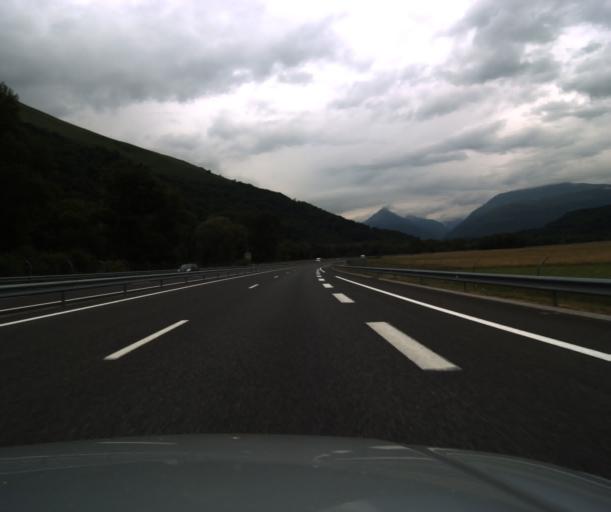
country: FR
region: Midi-Pyrenees
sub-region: Departement des Hautes-Pyrenees
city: Argeles-Gazost
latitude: 43.0361
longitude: -0.0639
